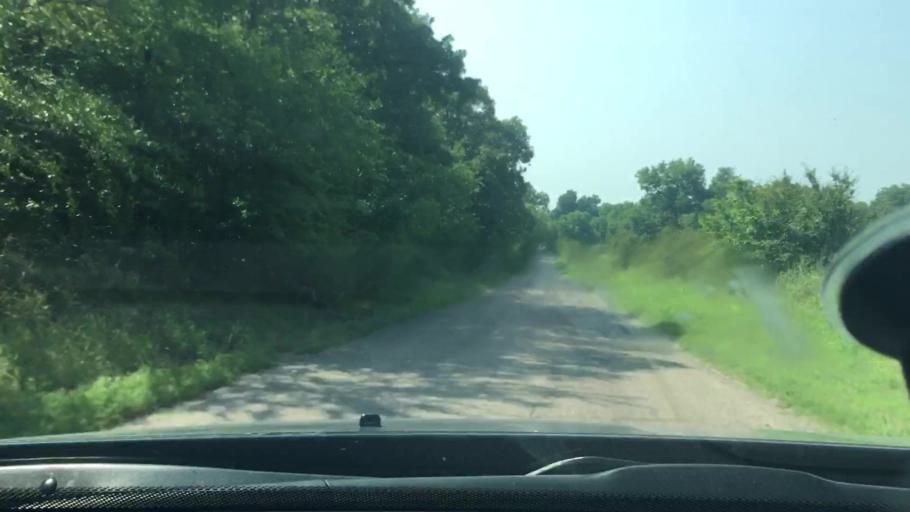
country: US
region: Oklahoma
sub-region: Pontotoc County
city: Ada
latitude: 34.6648
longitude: -96.5298
